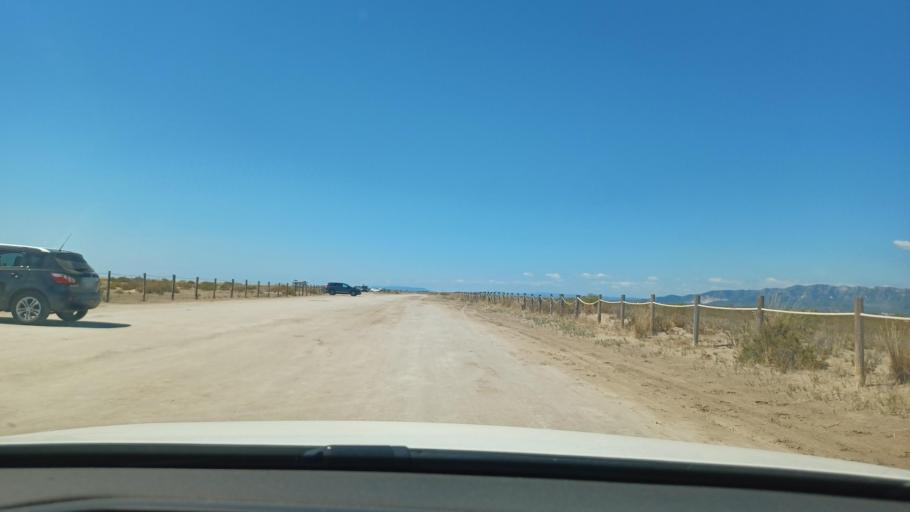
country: ES
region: Catalonia
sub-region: Provincia de Tarragona
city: Deltebre
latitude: 40.6438
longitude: 0.7591
